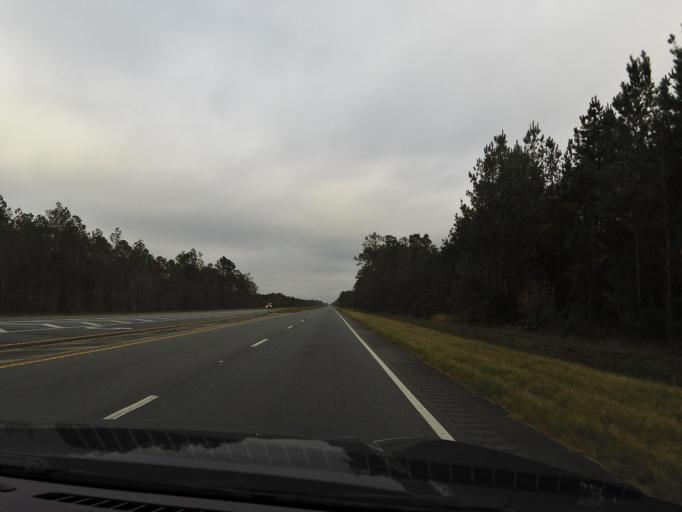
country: US
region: Georgia
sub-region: Charlton County
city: Folkston
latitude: 30.8934
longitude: -82.0526
